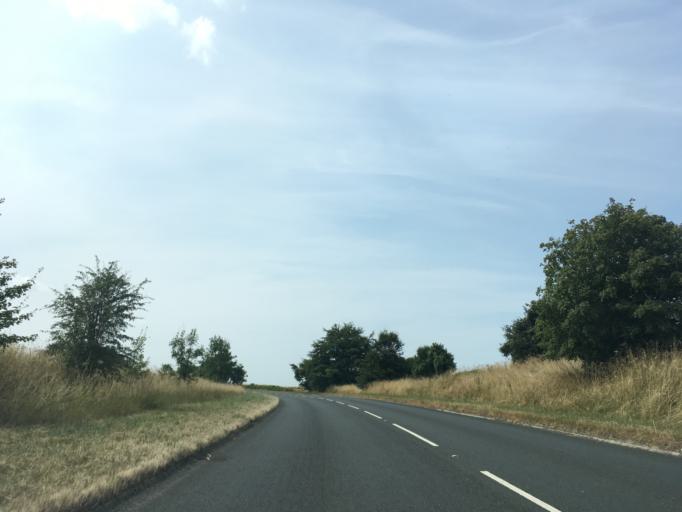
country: GB
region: England
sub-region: Gloucestershire
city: Nailsworth
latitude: 51.6668
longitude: -2.2302
